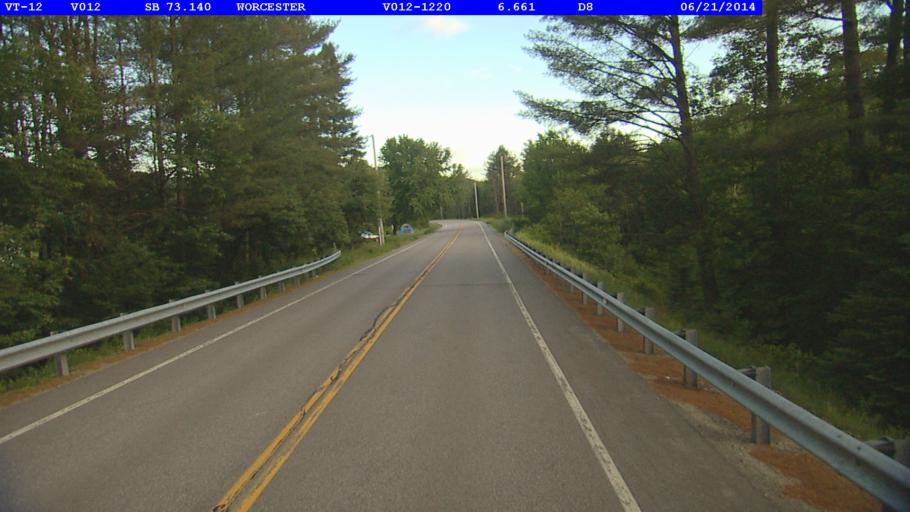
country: US
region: Vermont
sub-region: Lamoille County
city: Morrisville
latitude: 44.4373
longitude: -72.5359
